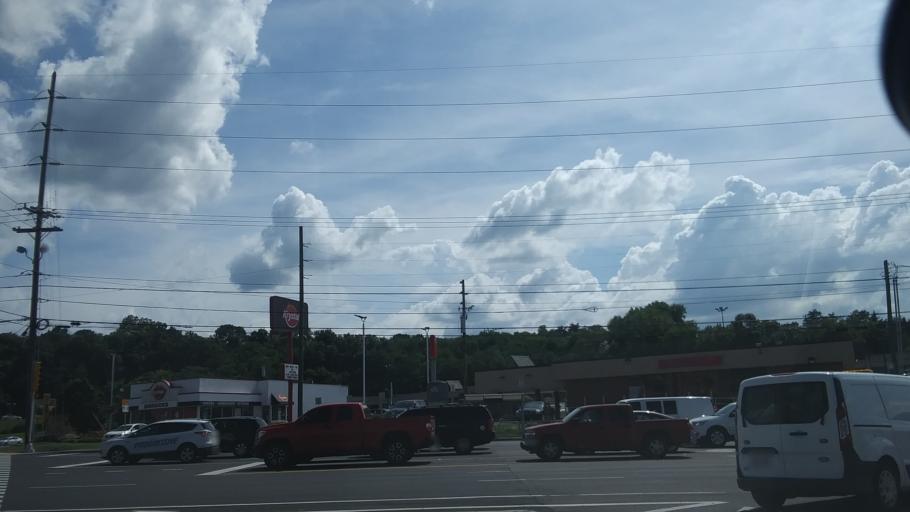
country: US
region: Tennessee
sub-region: Rutherford County
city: La Vergne
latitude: 36.0723
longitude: -86.6362
